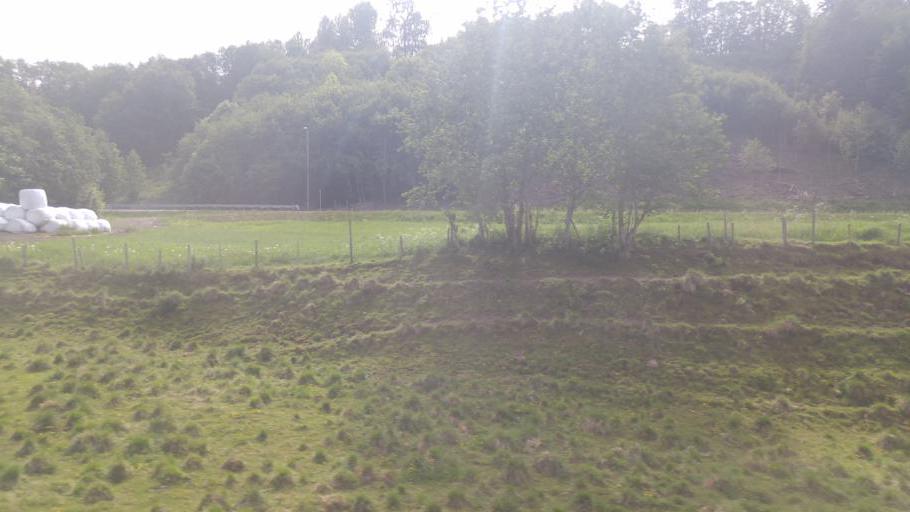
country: NO
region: Sor-Trondelag
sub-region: Melhus
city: Lundamo
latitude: 63.1325
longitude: 10.2469
